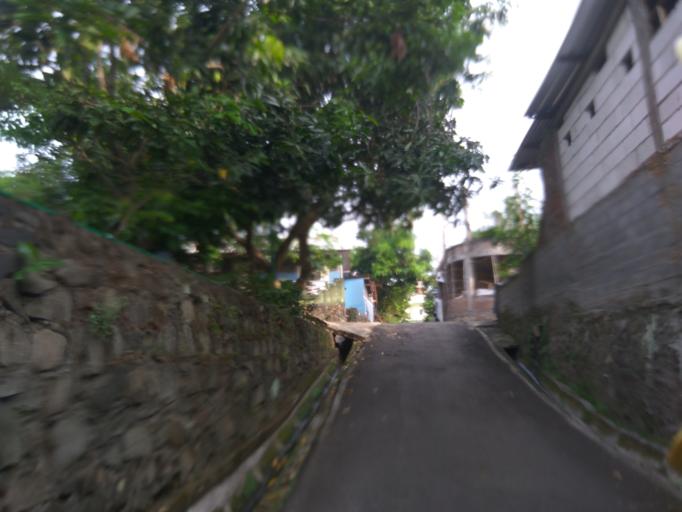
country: ID
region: Central Java
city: Semarang
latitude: -7.0309
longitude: 110.4418
